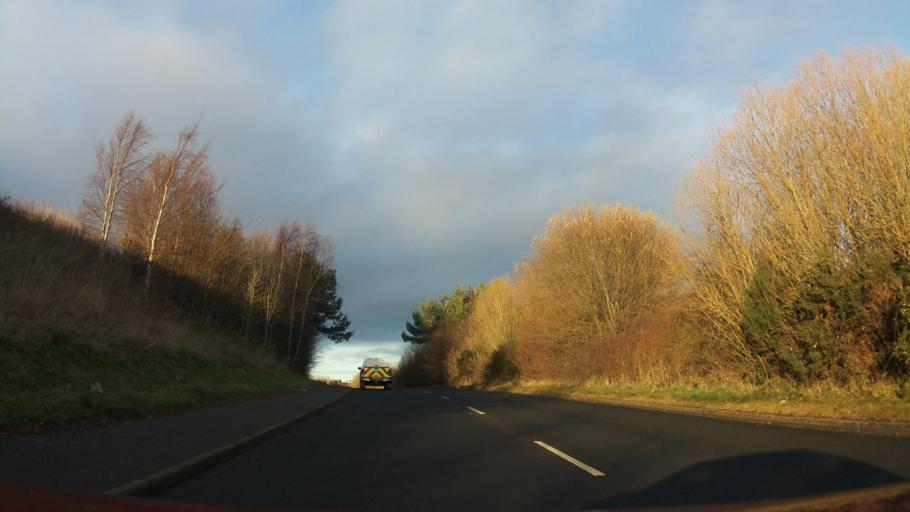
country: GB
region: Scotland
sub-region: Fife
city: Tayport
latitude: 56.4920
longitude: -2.8041
